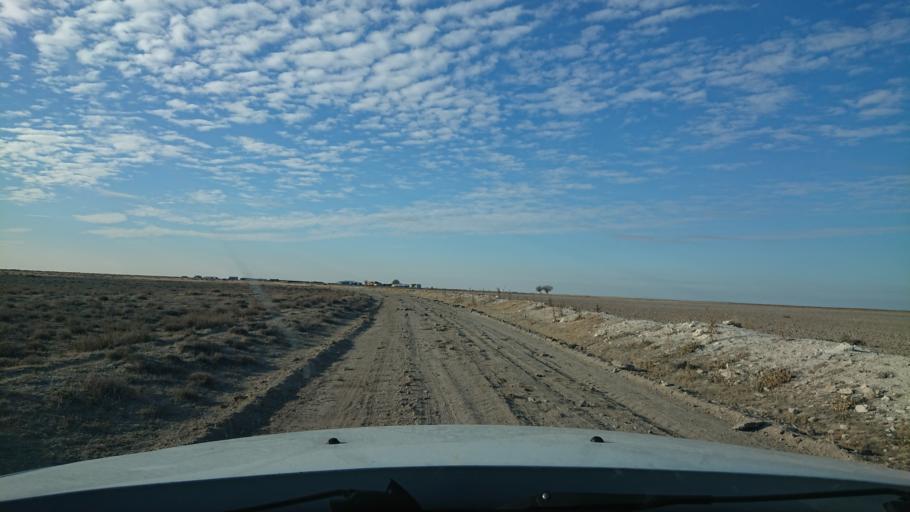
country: TR
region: Aksaray
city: Eskil
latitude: 38.5648
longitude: 33.3028
